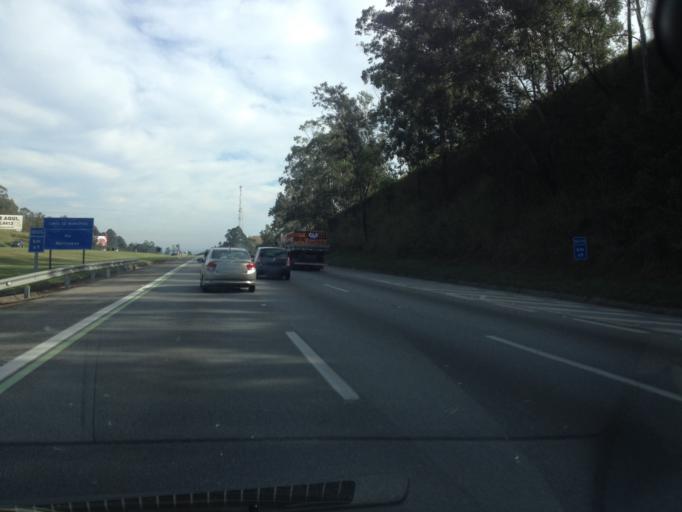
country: BR
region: Sao Paulo
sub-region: Mairinque
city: Mairinque
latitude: -23.4204
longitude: -47.2493
